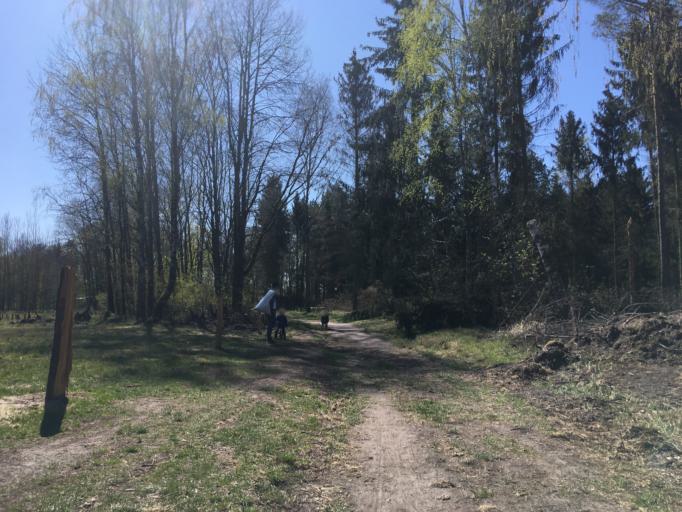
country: DE
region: Brandenburg
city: Wandlitz
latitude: 52.6869
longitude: 13.4647
